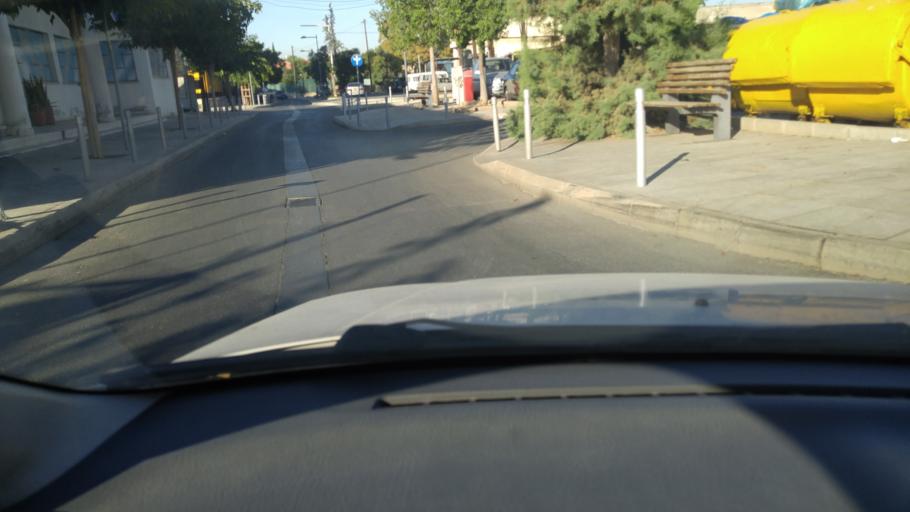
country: CY
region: Limassol
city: Limassol
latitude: 34.6736
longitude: 33.0391
